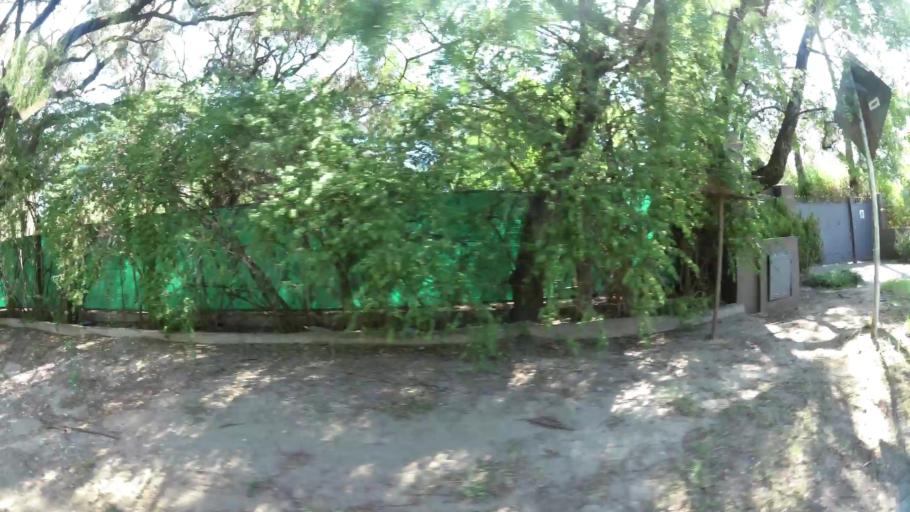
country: AR
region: Cordoba
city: Villa Allende
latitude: -31.2911
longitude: -64.2843
